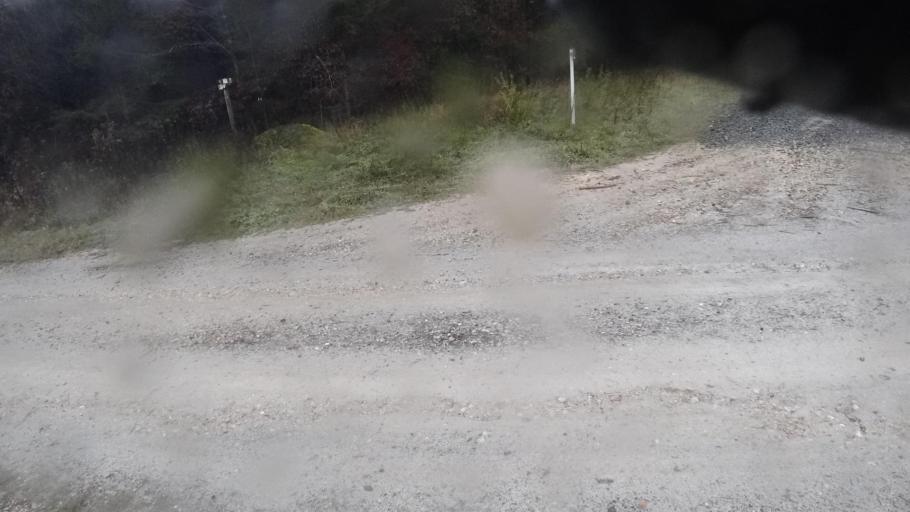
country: DE
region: Rheinland-Pfalz
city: Maisborn
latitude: 50.0963
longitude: 7.5941
